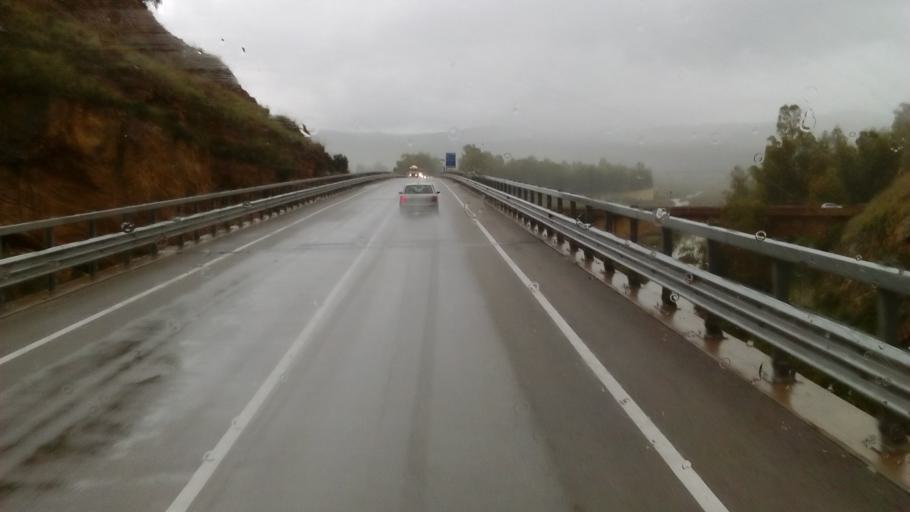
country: IT
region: Sicily
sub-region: Enna
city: Pietraperzia
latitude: 37.4970
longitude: 14.1441
